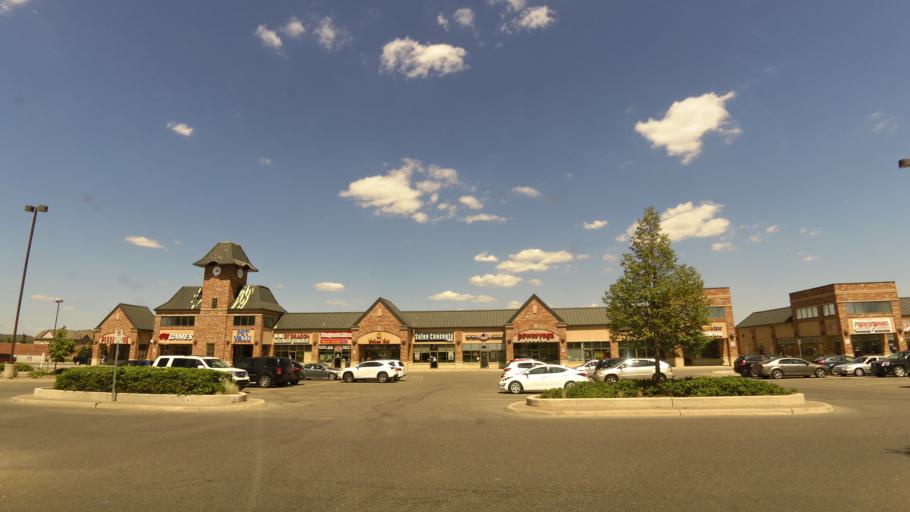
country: CA
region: Ontario
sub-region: Halton
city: Milton
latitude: 43.6311
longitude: -79.8761
